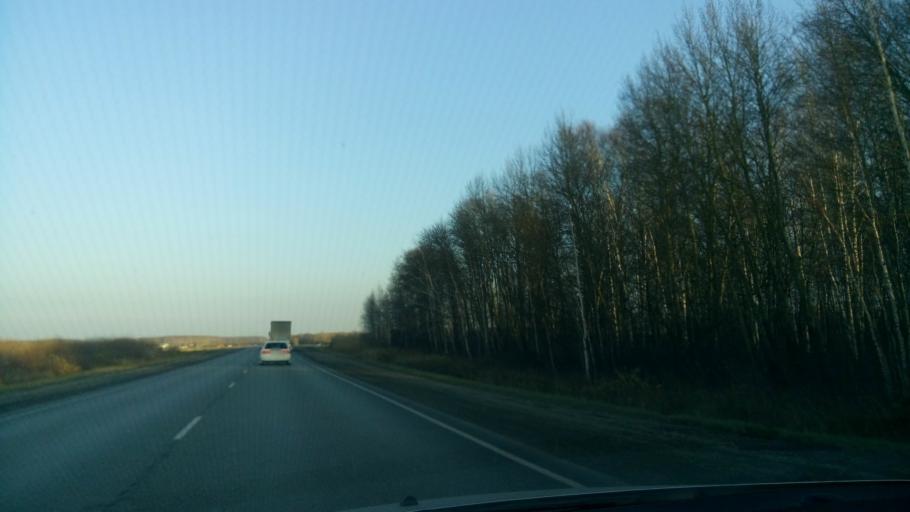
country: RU
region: Sverdlovsk
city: Baraba
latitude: 56.7720
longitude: 61.8989
